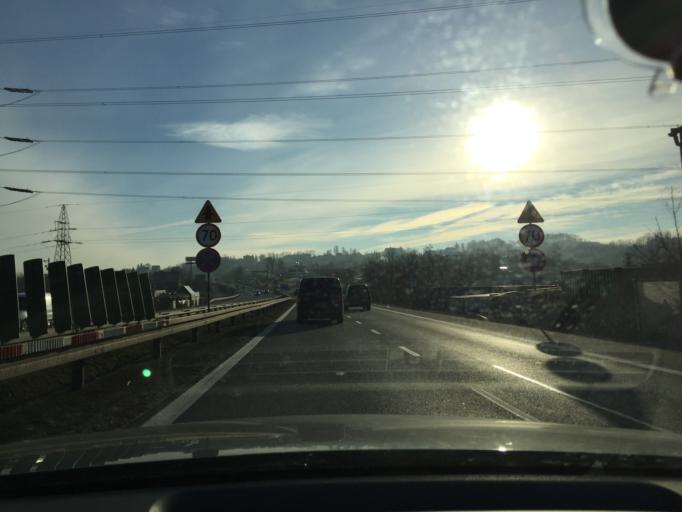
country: PL
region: Lesser Poland Voivodeship
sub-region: Powiat krakowski
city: Mogilany
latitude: 49.9533
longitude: 19.8899
